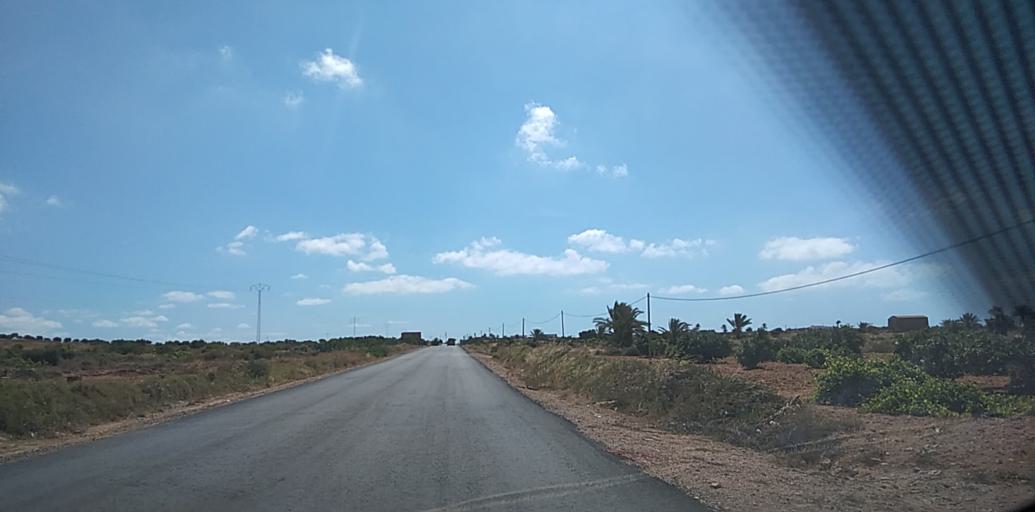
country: TN
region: Safaqis
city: Al Qarmadah
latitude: 34.6573
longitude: 11.0747
